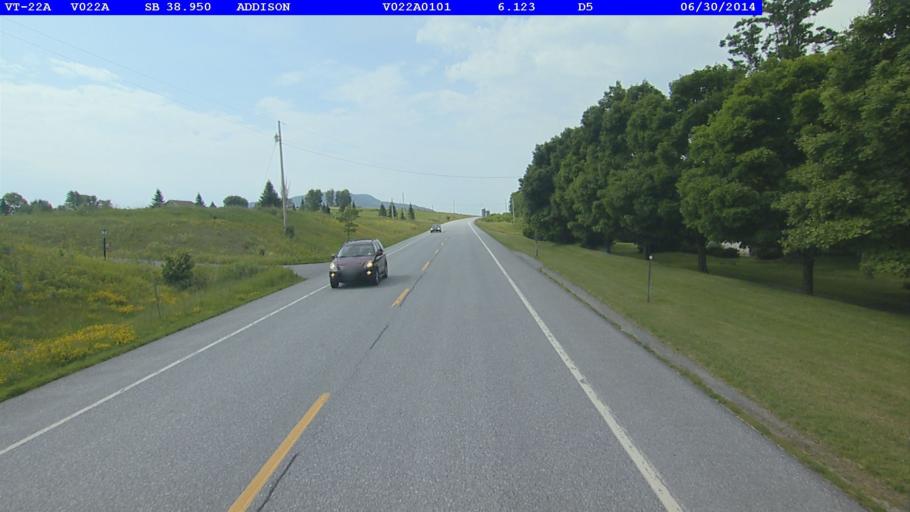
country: US
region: Vermont
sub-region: Addison County
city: Vergennes
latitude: 44.1168
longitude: -73.2936
